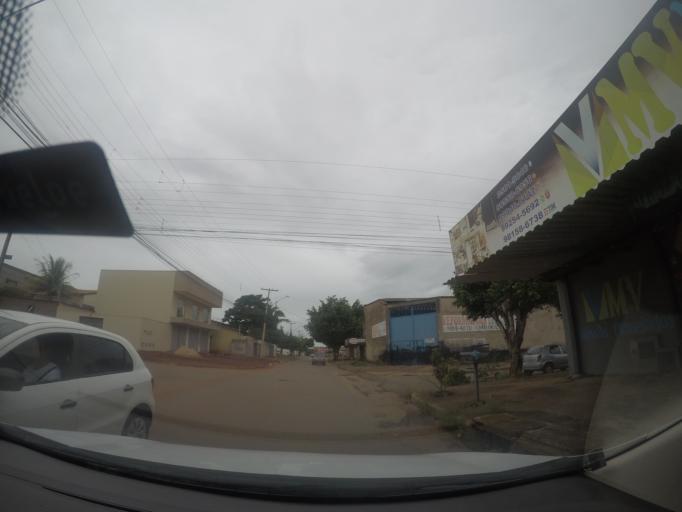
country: BR
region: Goias
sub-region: Goiania
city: Goiania
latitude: -16.6690
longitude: -49.3219
